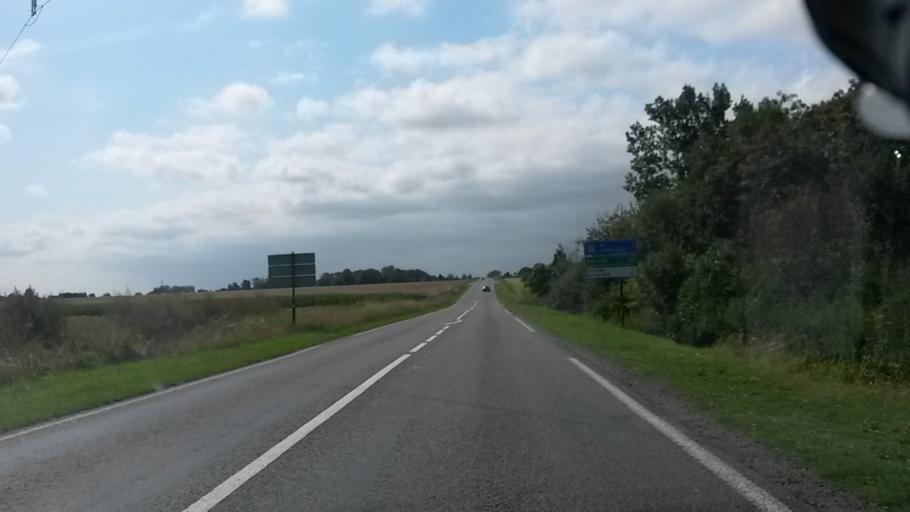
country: FR
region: Nord-Pas-de-Calais
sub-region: Departement du Pas-de-Calais
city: Vaulx-Vraucourt
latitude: 50.1231
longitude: 2.9506
